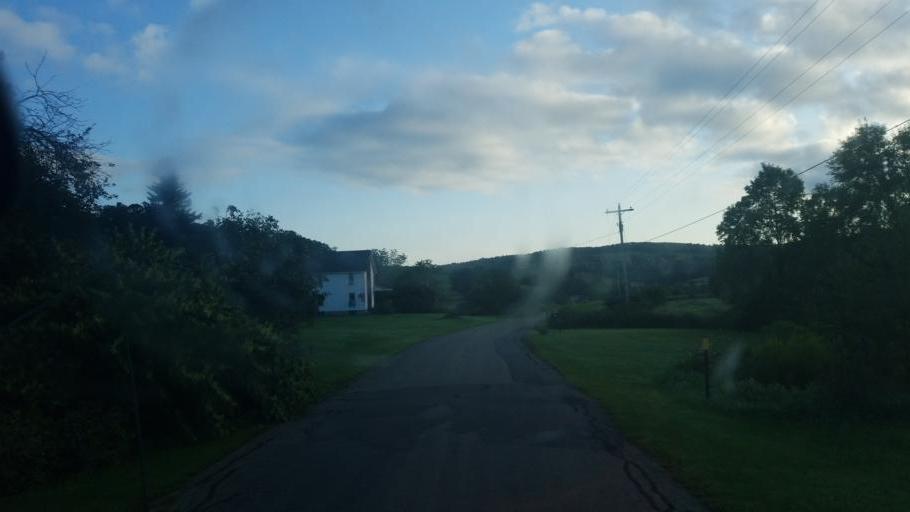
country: US
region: Pennsylvania
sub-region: Potter County
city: Galeton
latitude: 41.8882
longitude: -77.8086
